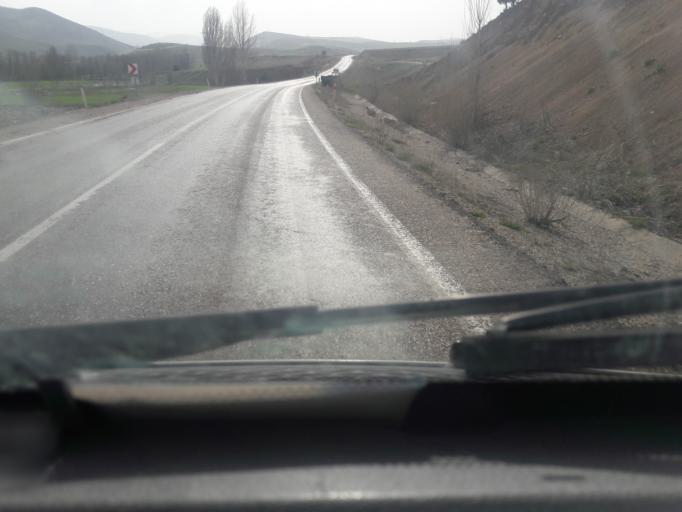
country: TR
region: Gumushane
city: Kelkit
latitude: 40.1262
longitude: 39.3511
